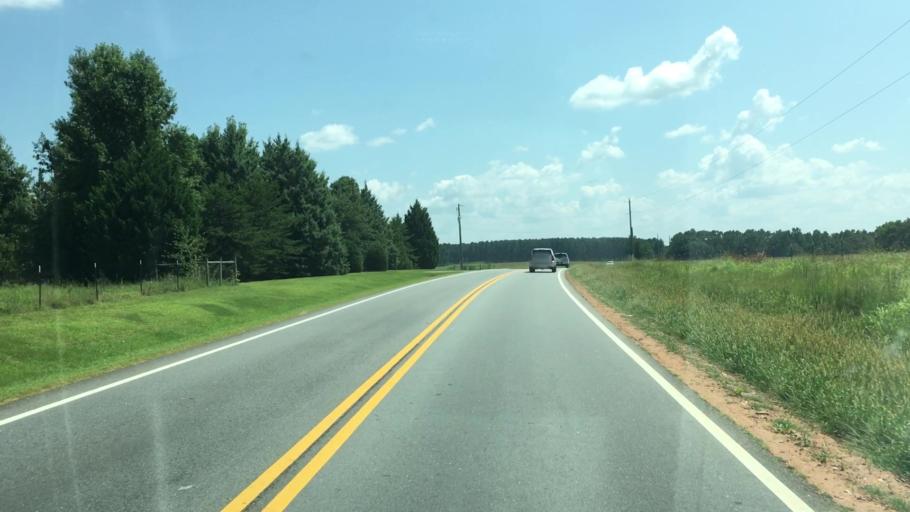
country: US
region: Georgia
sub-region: Oconee County
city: Watkinsville
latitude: 33.7991
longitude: -83.4259
